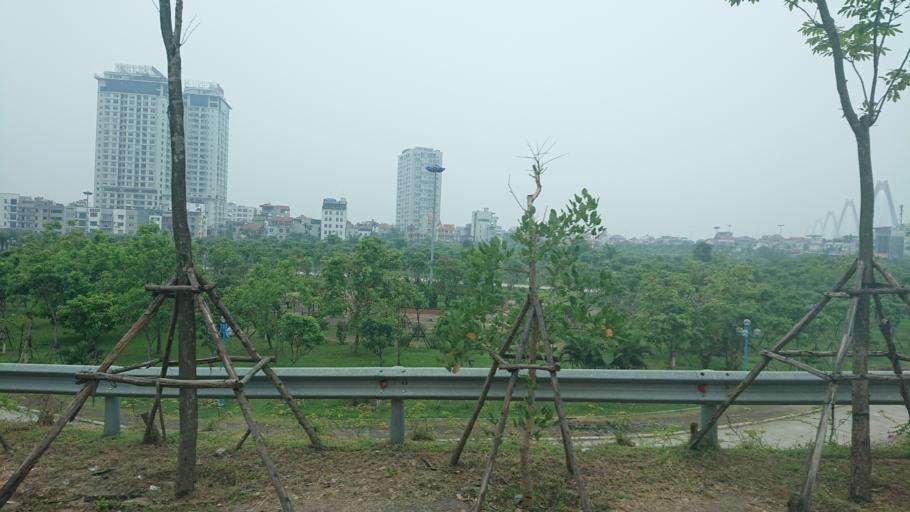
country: VN
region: Ha Noi
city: Tay Ho
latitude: 21.0825
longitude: 105.8147
